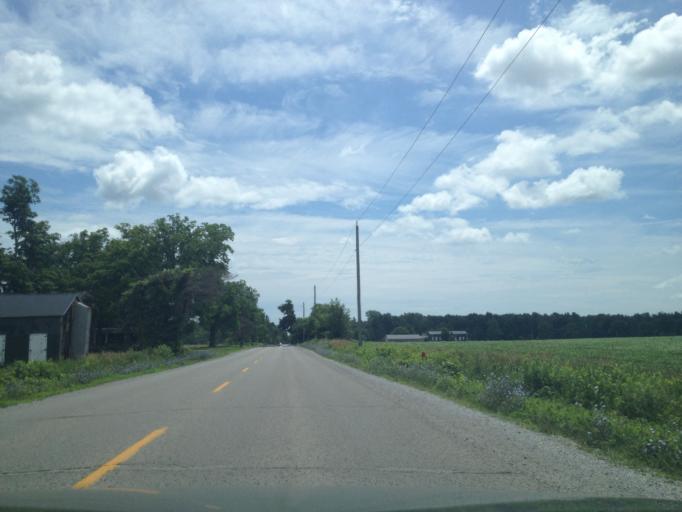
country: CA
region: Ontario
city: Norfolk County
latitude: 42.8123
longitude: -80.3221
